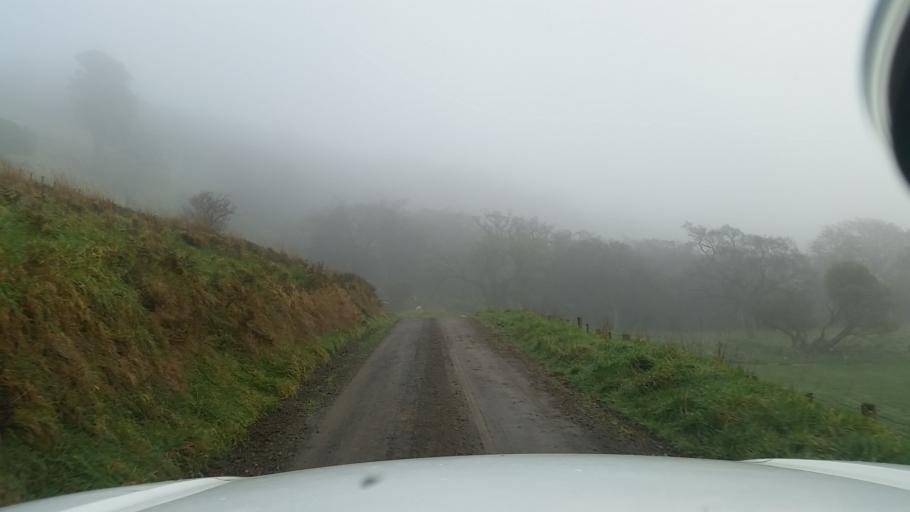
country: NZ
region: Canterbury
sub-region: Christchurch City
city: Christchurch
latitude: -43.7396
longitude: 172.8857
